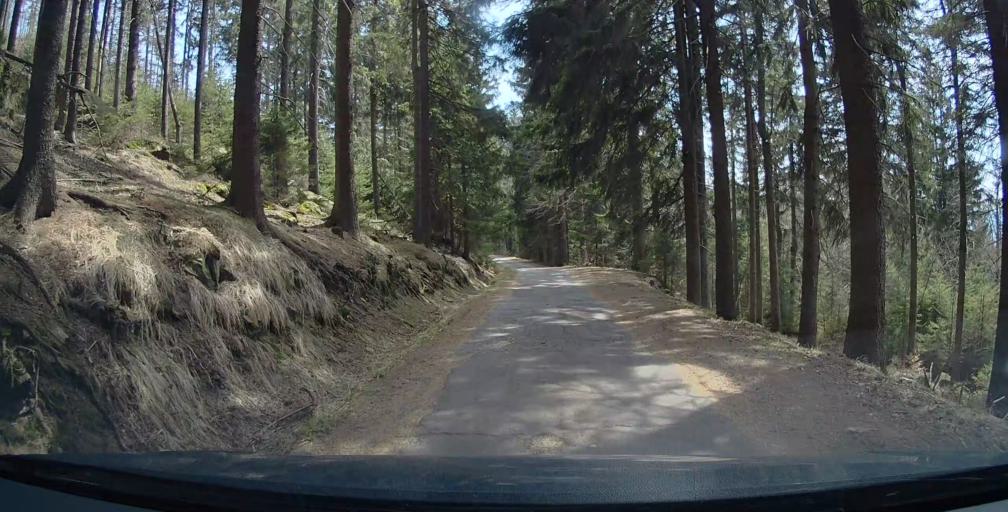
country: CZ
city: Machov
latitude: 50.4717
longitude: 16.2884
